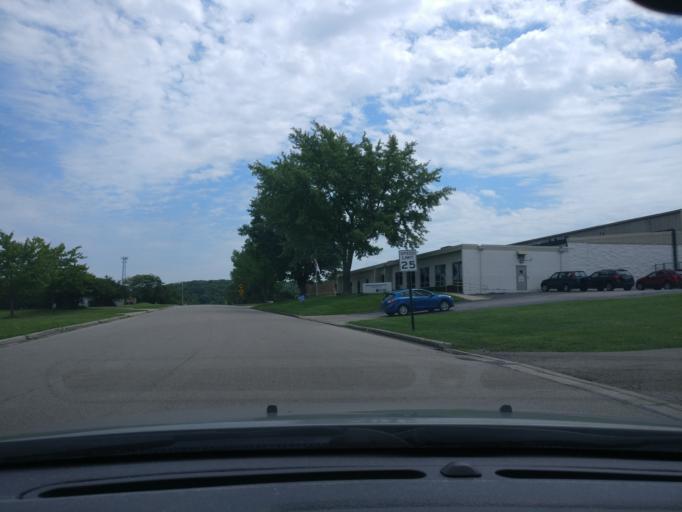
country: US
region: Ohio
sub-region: Montgomery County
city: West Carrollton City
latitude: 39.6540
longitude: -84.2421
